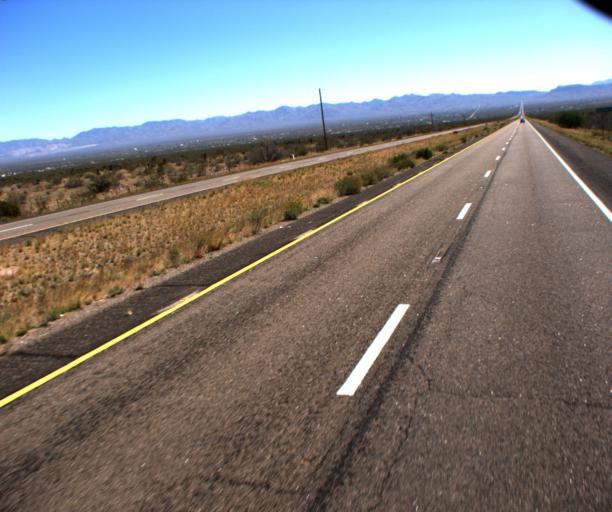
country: US
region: Arizona
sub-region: Mohave County
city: Golden Valley
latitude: 35.2278
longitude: -114.3395
